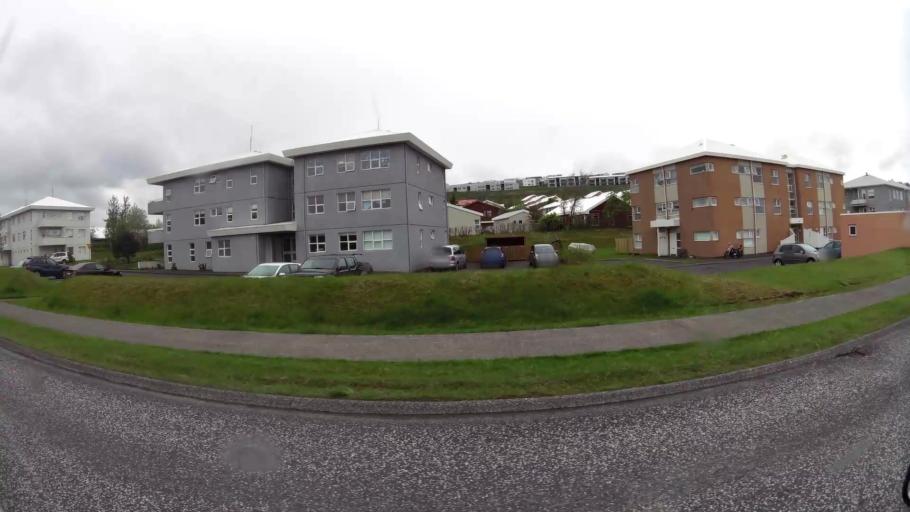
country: IS
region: Capital Region
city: Hafnarfjoerdur
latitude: 64.0599
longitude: -21.9301
